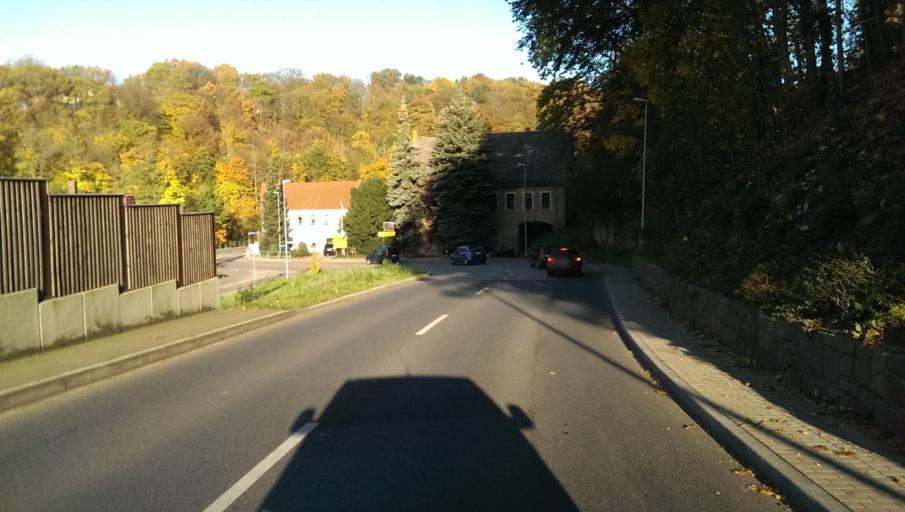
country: DE
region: Saxony
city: Mittweida
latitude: 50.9839
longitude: 12.9944
